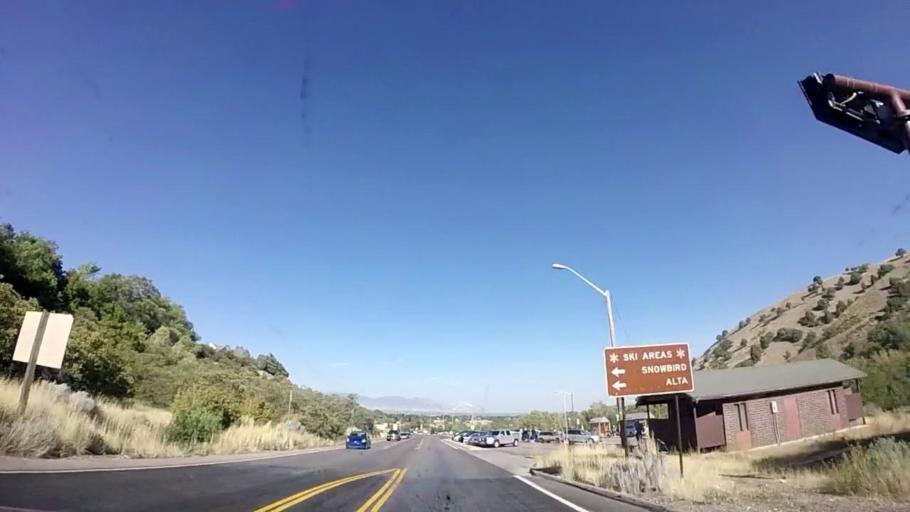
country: US
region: Utah
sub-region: Salt Lake County
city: Cottonwood Heights
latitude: 40.6191
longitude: -111.7859
